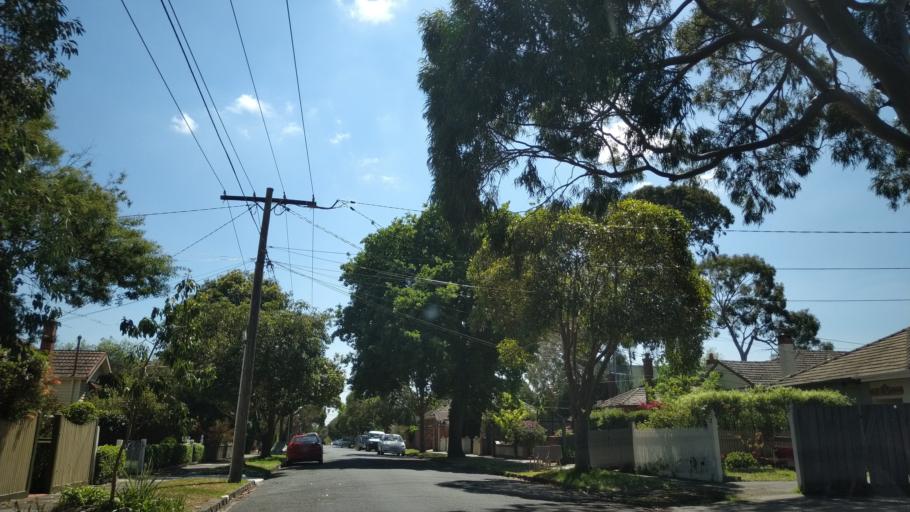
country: AU
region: Victoria
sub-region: Glen Eira
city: Glen Huntly
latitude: -37.8917
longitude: 145.0384
